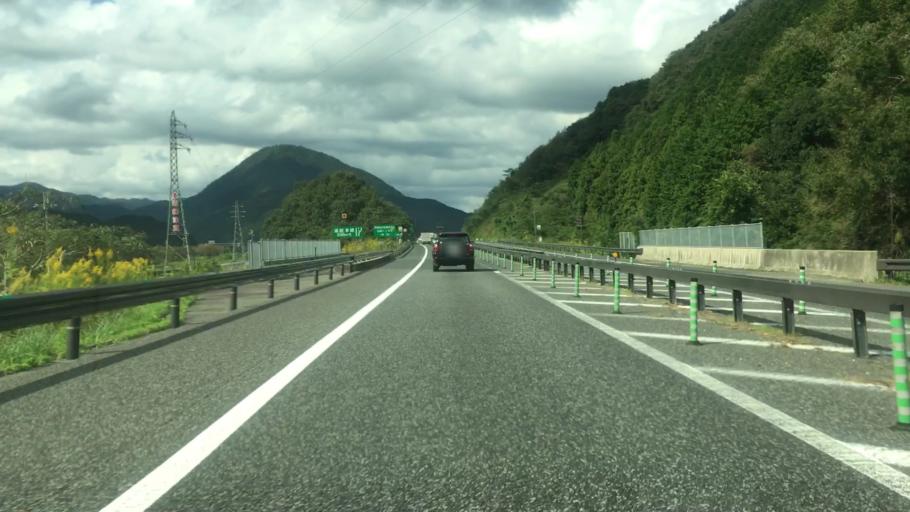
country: JP
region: Kyoto
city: Fukuchiyama
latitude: 35.2349
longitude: 135.0192
